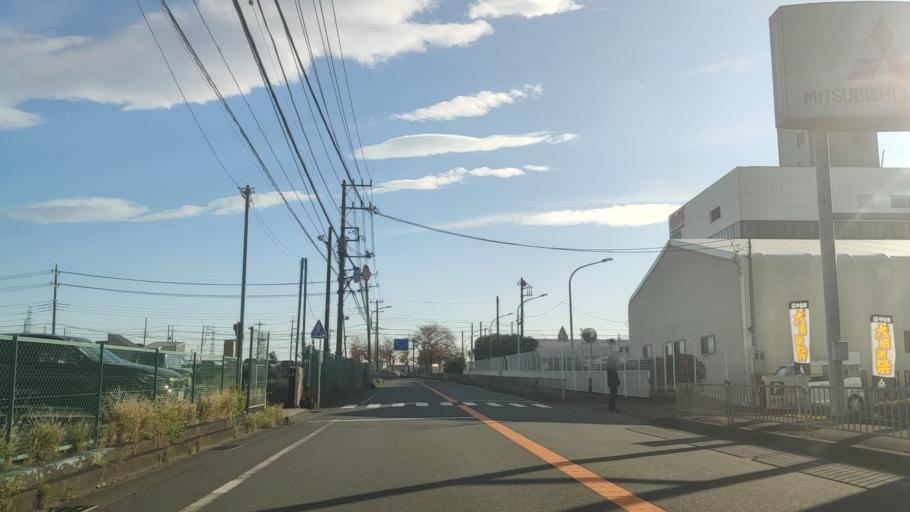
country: JP
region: Kanagawa
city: Atsugi
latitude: 35.4232
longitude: 139.3876
